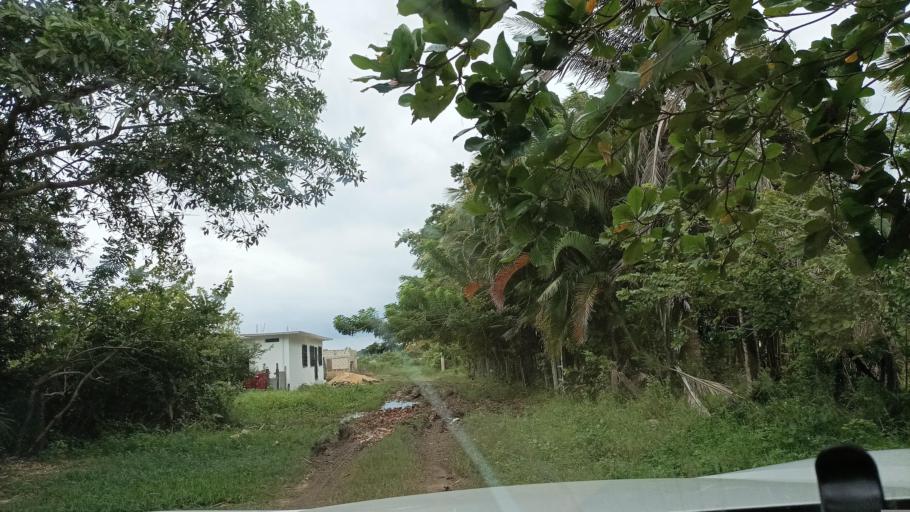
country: MX
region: Veracruz
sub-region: Coatzacoalcos
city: Fraccionamiento Ciudad Olmeca
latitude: 18.1814
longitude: -94.5929
